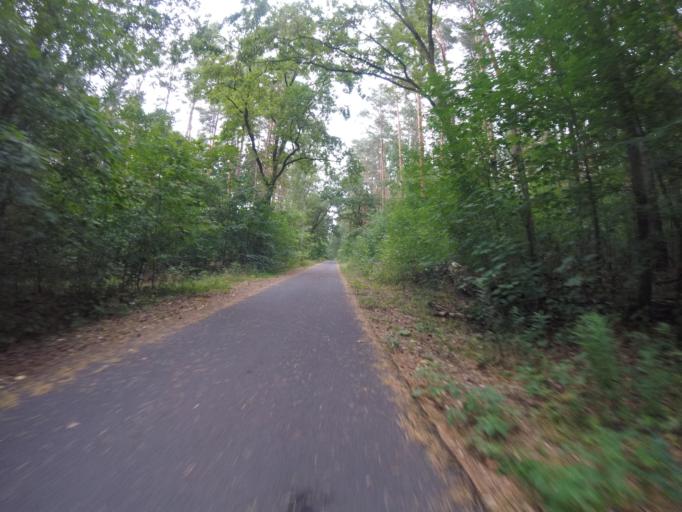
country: DE
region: Brandenburg
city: Oranienburg
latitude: 52.7897
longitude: 13.2951
